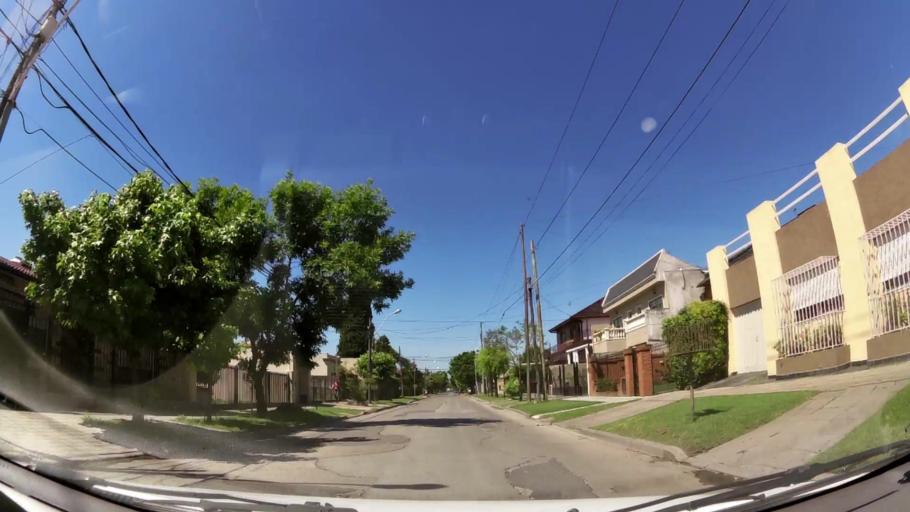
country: AR
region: Buenos Aires
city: Ituzaingo
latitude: -34.6643
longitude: -58.6594
